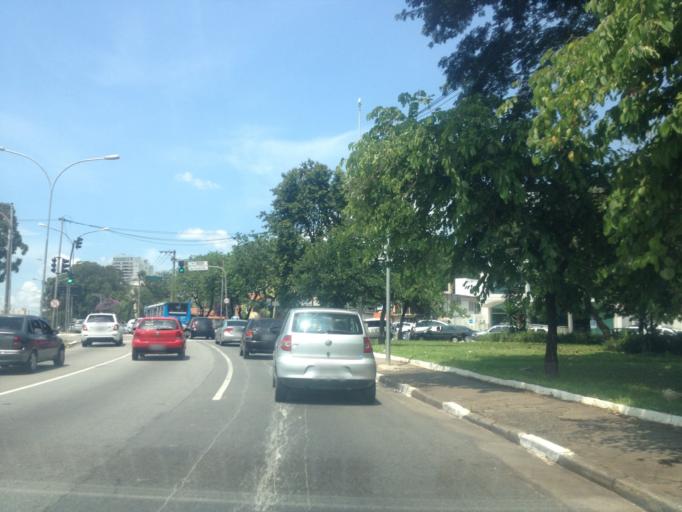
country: BR
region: Sao Paulo
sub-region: Diadema
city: Diadema
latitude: -23.6529
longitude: -46.6799
